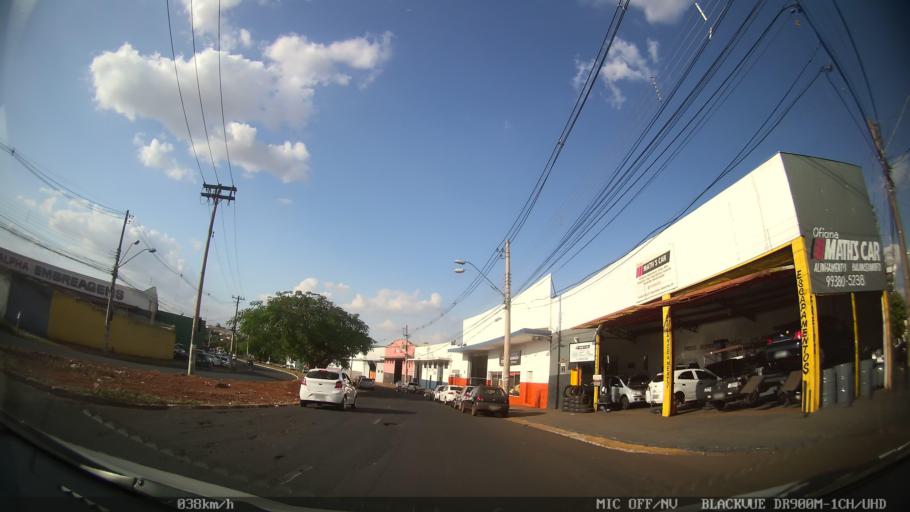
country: BR
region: Sao Paulo
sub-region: Ribeirao Preto
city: Ribeirao Preto
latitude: -21.1484
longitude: -47.8014
